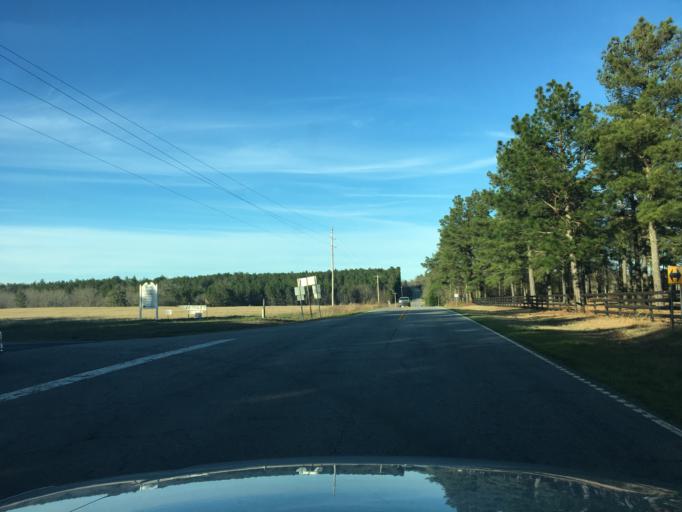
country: US
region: South Carolina
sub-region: Lexington County
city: Batesburg
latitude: 33.7990
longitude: -81.6402
